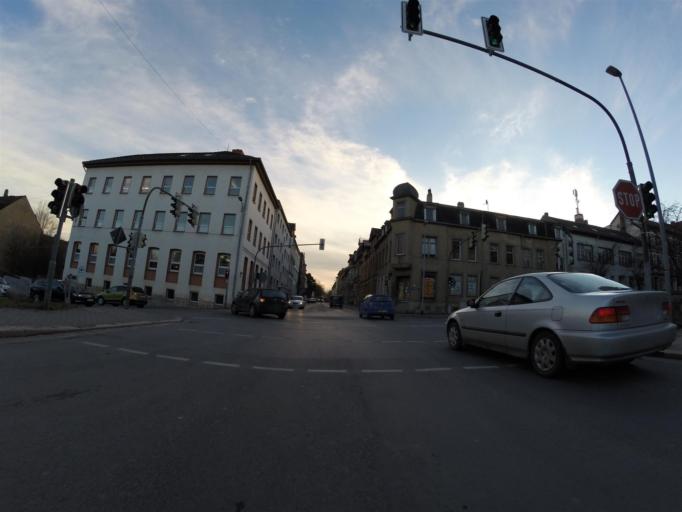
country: DE
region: Thuringia
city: Apolda
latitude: 51.0219
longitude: 11.5089
